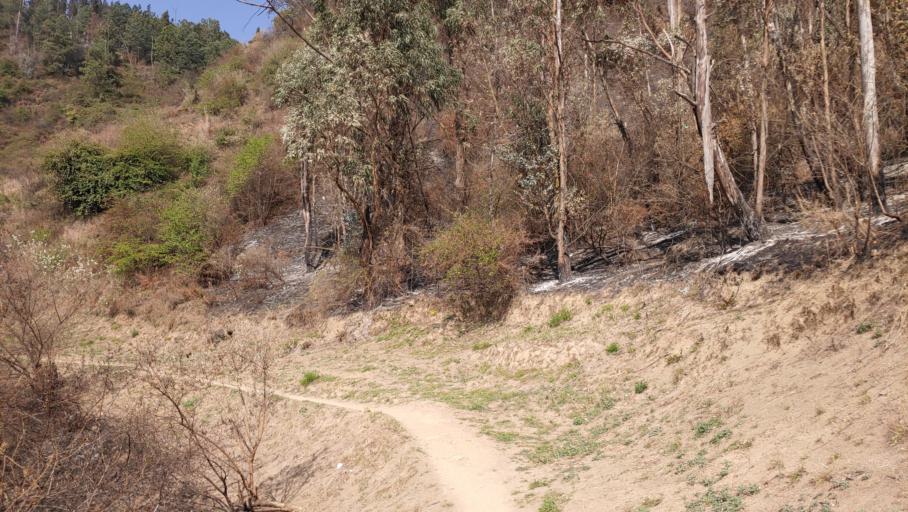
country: CN
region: Yunnan
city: Majie
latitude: 25.0485
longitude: 102.6190
